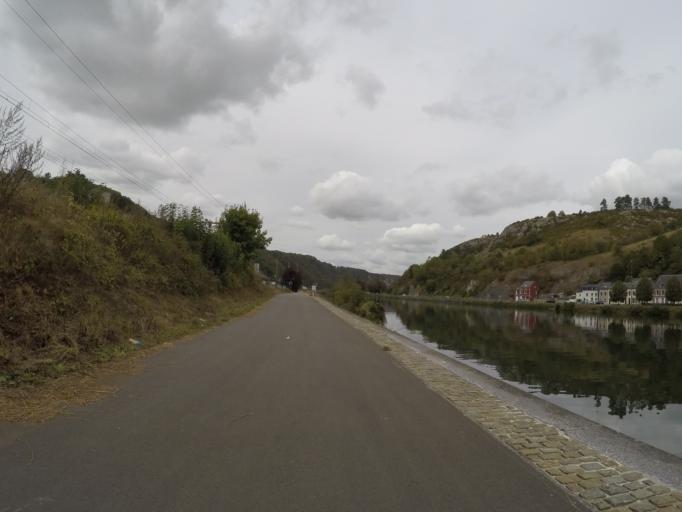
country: BE
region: Wallonia
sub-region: Province de Namur
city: Dinant
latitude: 50.2720
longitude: 4.9006
